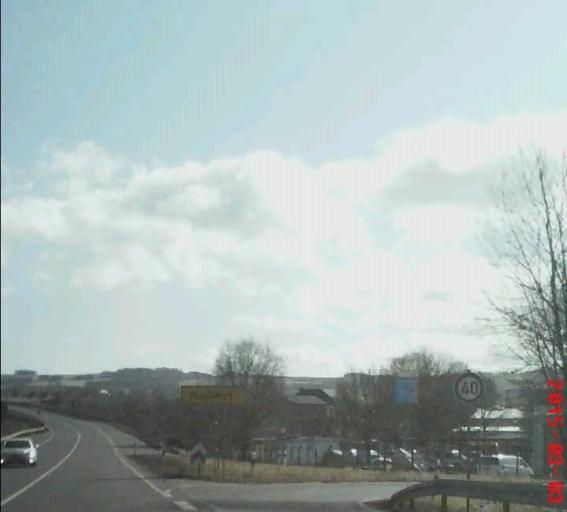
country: DE
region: Thuringia
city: Saalfeld
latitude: 50.6602
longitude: 11.3639
